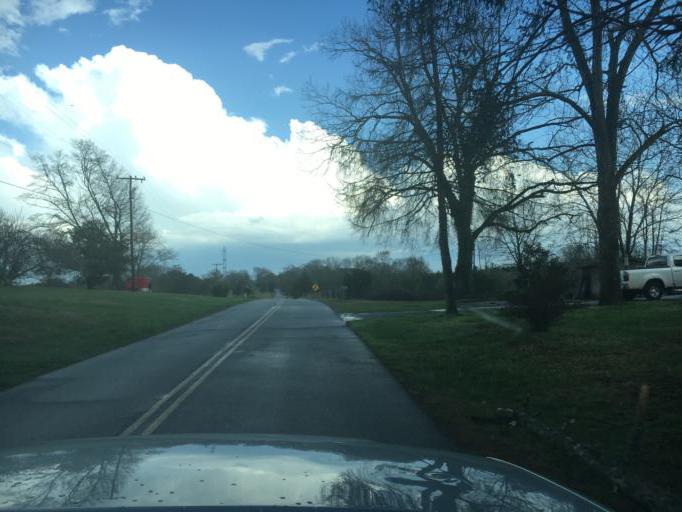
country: US
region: South Carolina
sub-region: Greenville County
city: Berea
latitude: 34.8660
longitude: -82.5122
